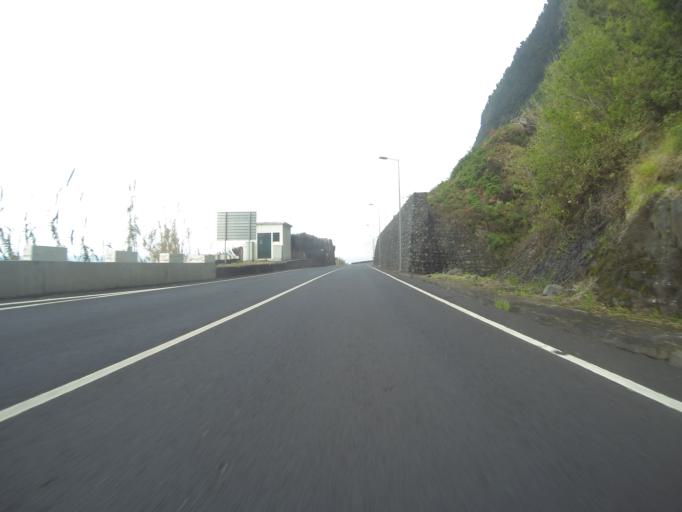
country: PT
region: Madeira
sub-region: Sao Vicente
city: Sao Vicente
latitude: 32.8135
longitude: -17.0722
